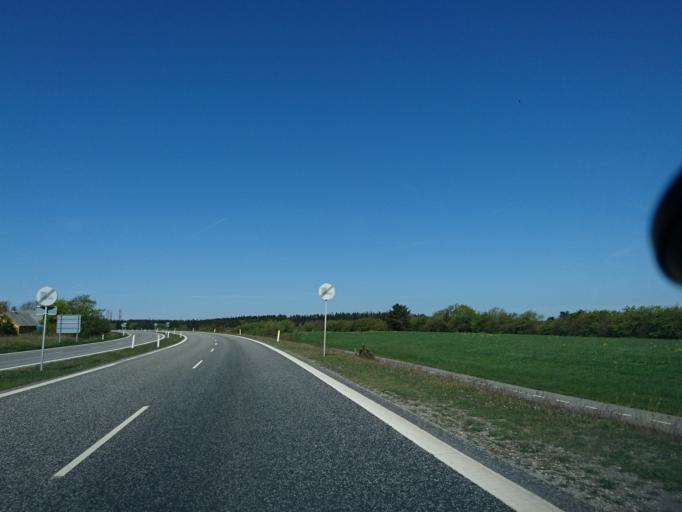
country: DK
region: North Denmark
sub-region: Hjorring Kommune
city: Hirtshals
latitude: 57.5663
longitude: 10.0139
